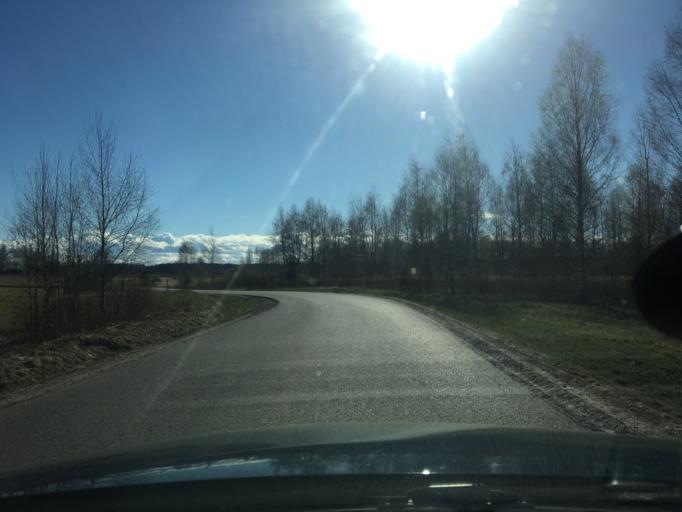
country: LV
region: Salaspils
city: Salaspils
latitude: 56.8741
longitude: 24.3257
